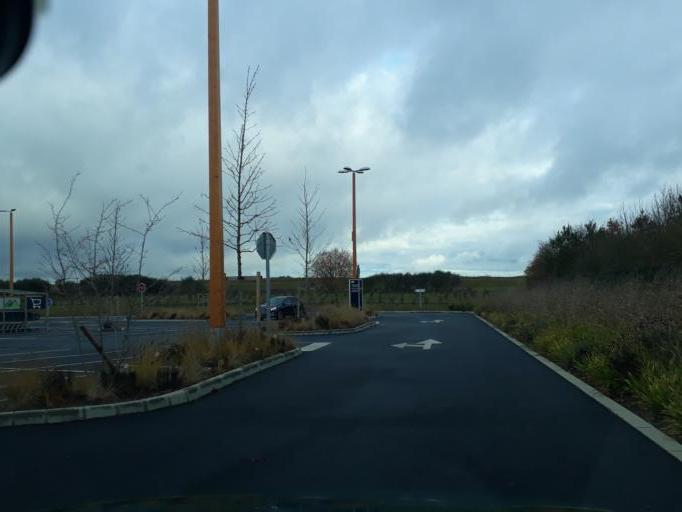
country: FR
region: Centre
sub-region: Departement du Loir-et-Cher
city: Villebarou
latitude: 47.6155
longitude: 1.3223
